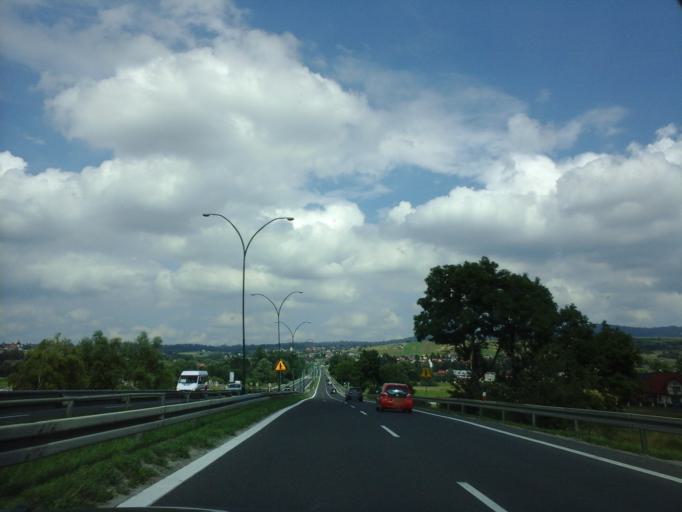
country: PL
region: Lesser Poland Voivodeship
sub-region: Powiat nowotarski
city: Nowy Targ
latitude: 49.4810
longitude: 20.0212
